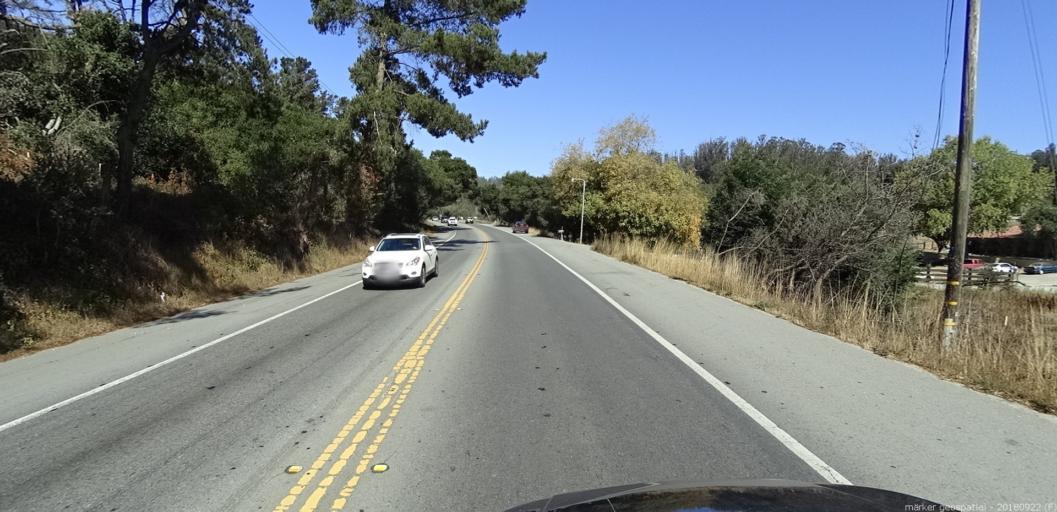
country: US
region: California
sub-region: Monterey County
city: Prunedale
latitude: 36.8055
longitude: -121.6684
